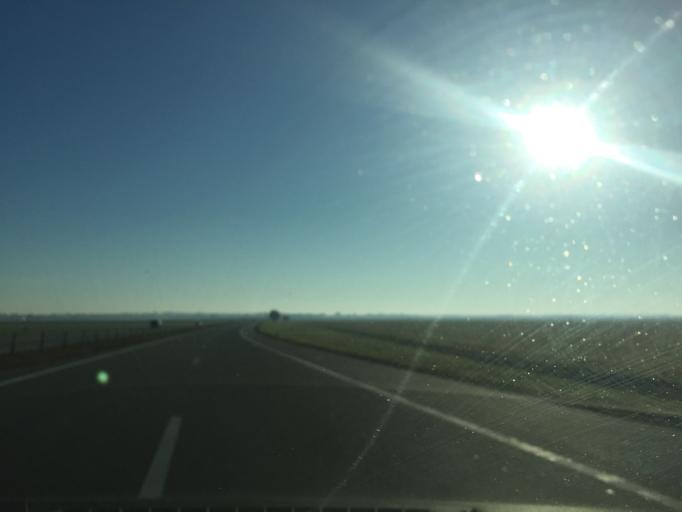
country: BY
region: Minsk
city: Smilavichy
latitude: 53.7615
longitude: 27.9392
